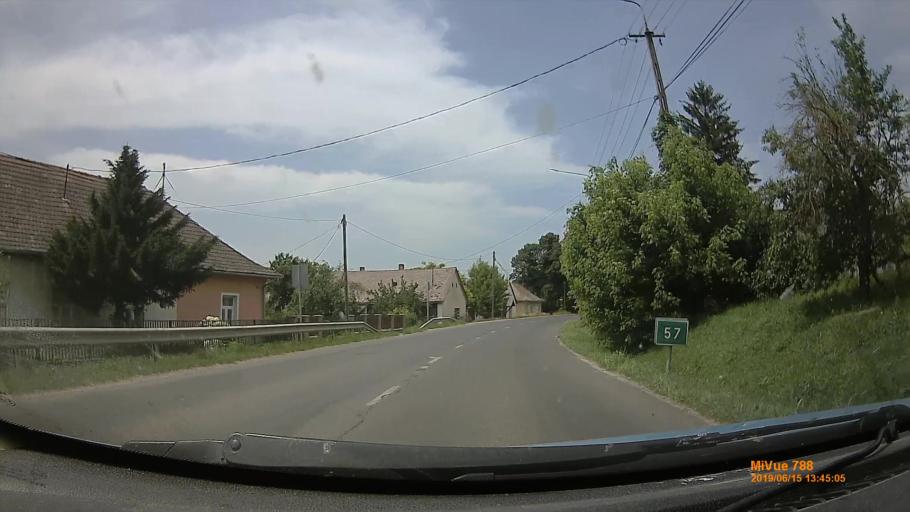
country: HU
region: Tolna
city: Iregszemcse
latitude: 46.6896
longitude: 18.1878
